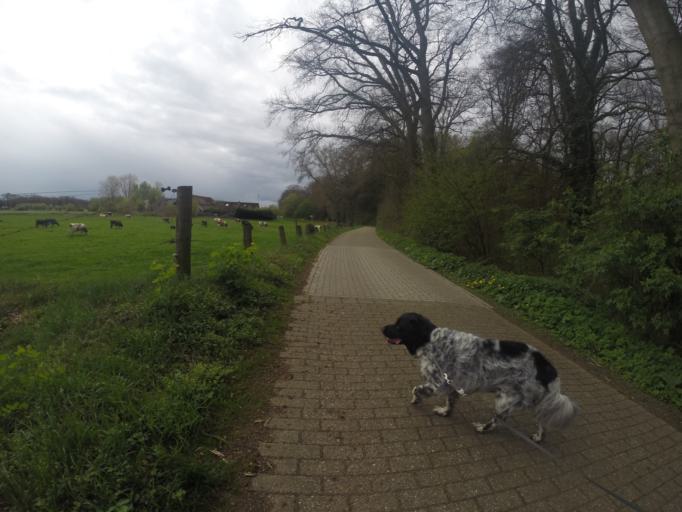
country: NL
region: Gelderland
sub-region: Gemeente Zutphen
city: Leesten
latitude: 52.1001
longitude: 6.2645
